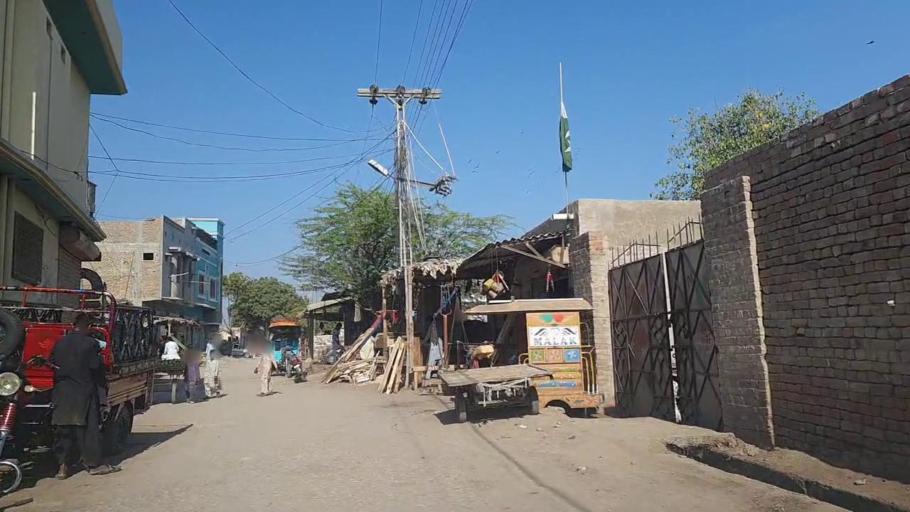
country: PK
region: Sindh
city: Digri
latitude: 25.0738
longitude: 69.2158
